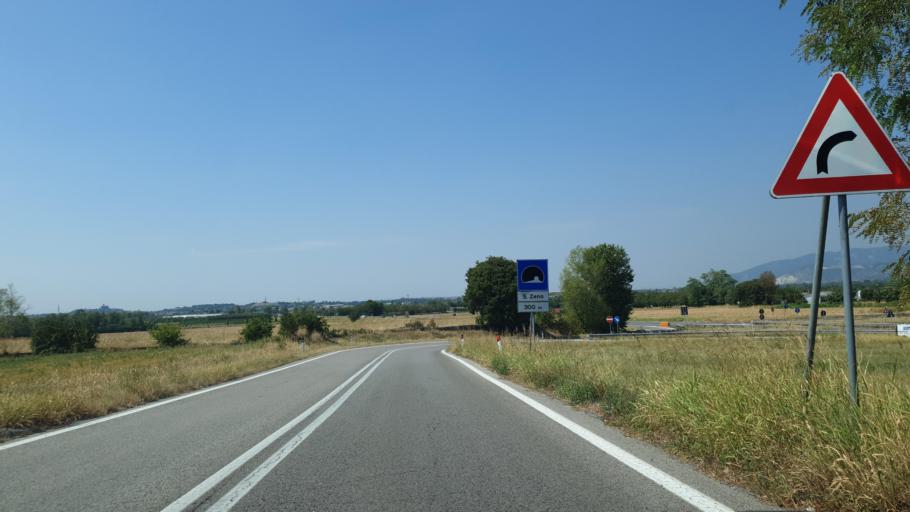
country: IT
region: Lombardy
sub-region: Provincia di Brescia
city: Lonato
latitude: 45.4739
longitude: 10.4704
